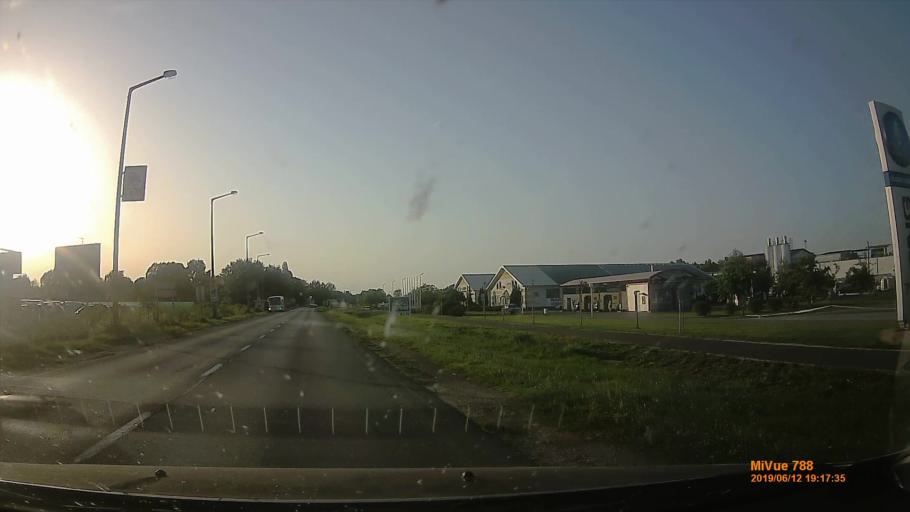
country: HU
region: Bacs-Kiskun
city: Kecskemet
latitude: 46.8828
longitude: 19.7064
